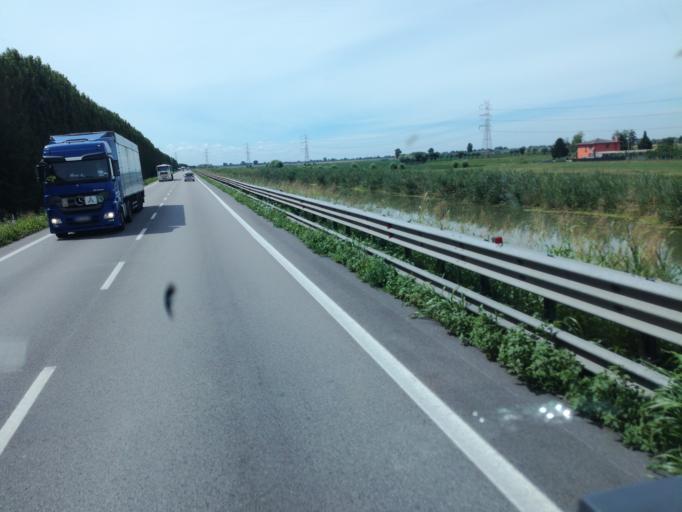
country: IT
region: Veneto
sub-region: Provincia di Padova
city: Codevigo
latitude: 45.2731
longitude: 12.1290
